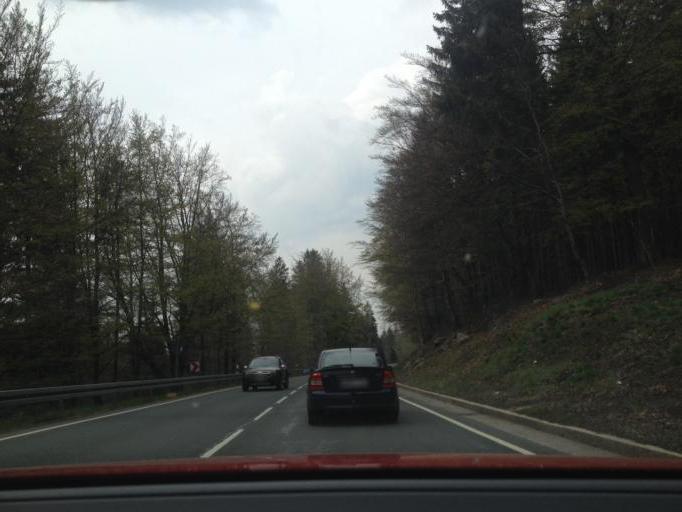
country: DE
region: Bavaria
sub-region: Upper Franconia
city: Nagel
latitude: 50.0052
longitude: 11.8918
